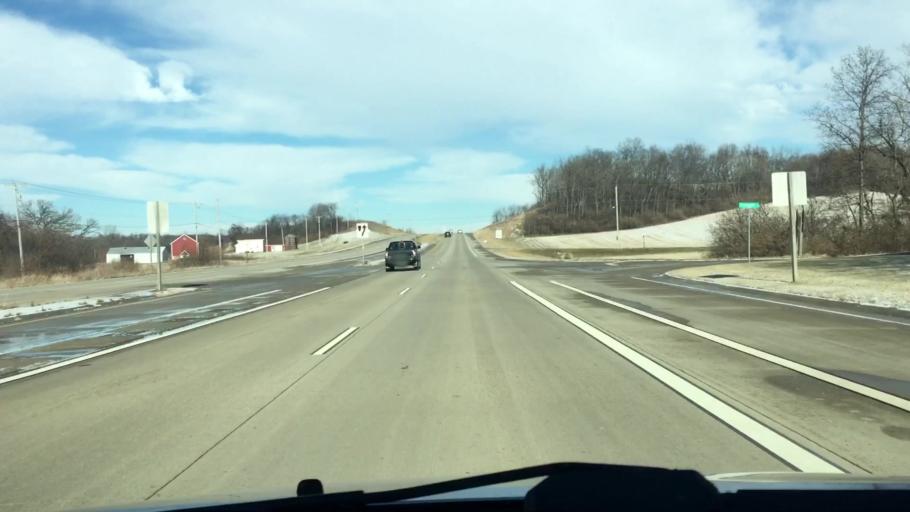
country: US
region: Wisconsin
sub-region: Waukesha County
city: Mukwonago
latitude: 42.9035
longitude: -88.3453
